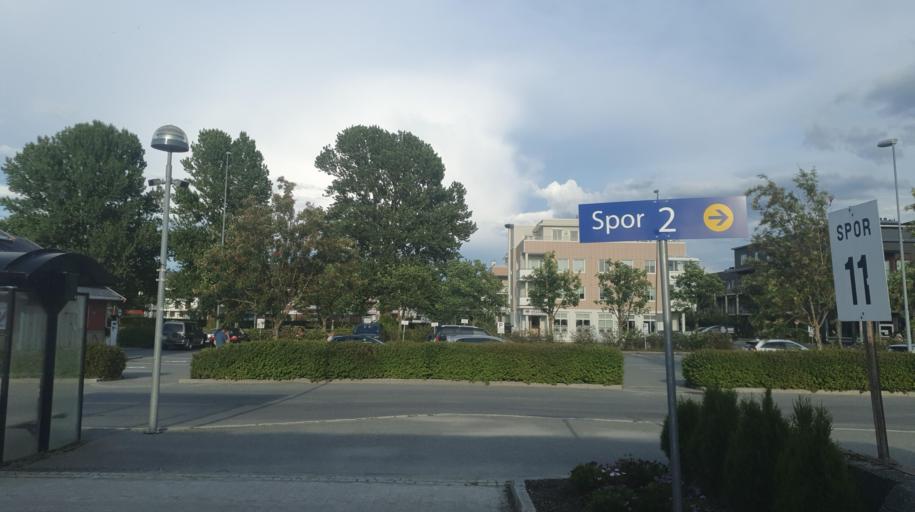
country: NO
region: Nord-Trondelag
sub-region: Stjordal
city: Stjordal
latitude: 63.4699
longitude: 10.9136
